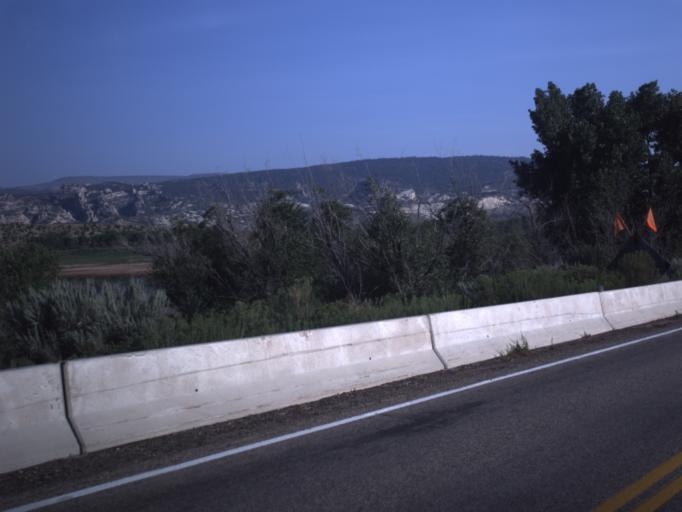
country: US
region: Utah
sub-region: Uintah County
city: Vernal
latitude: 40.5226
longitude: -109.5219
